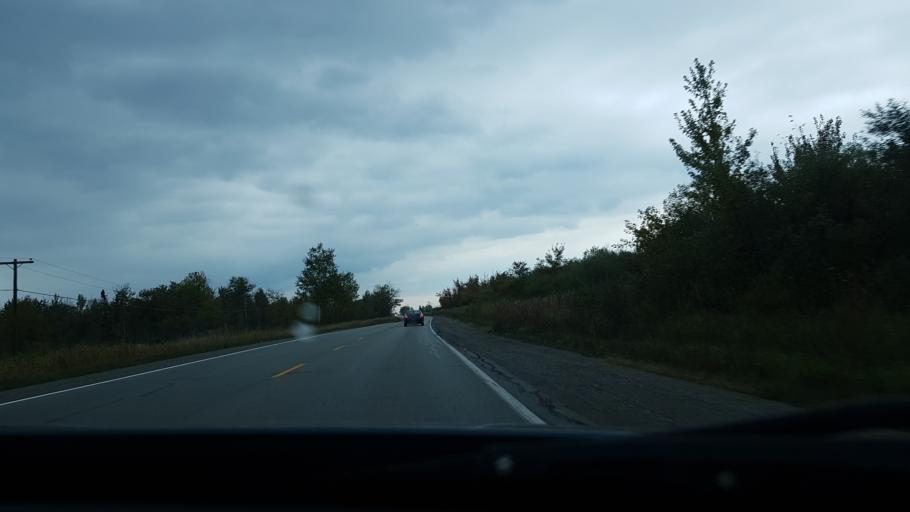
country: CA
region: Ontario
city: Omemee
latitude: 44.3688
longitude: -78.6785
